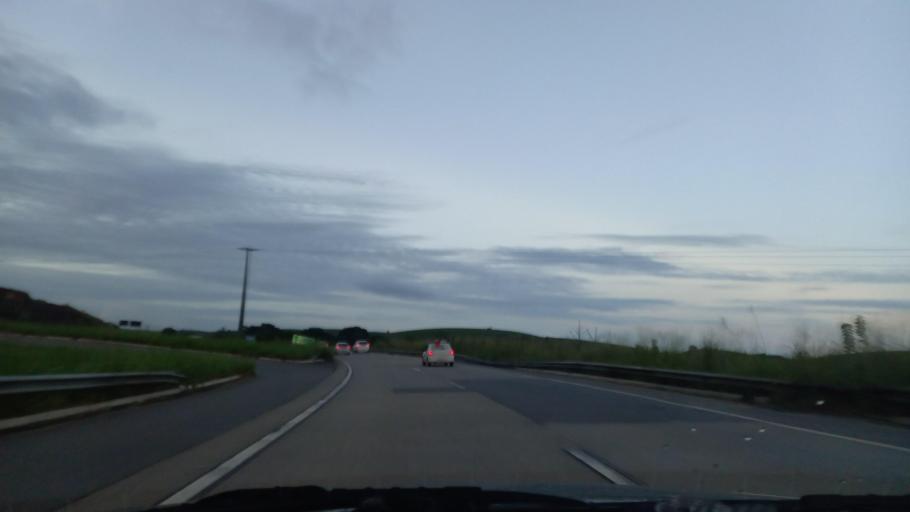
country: BR
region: Pernambuco
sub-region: Gameleira
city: Gameleira
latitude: -8.5539
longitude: -35.3957
